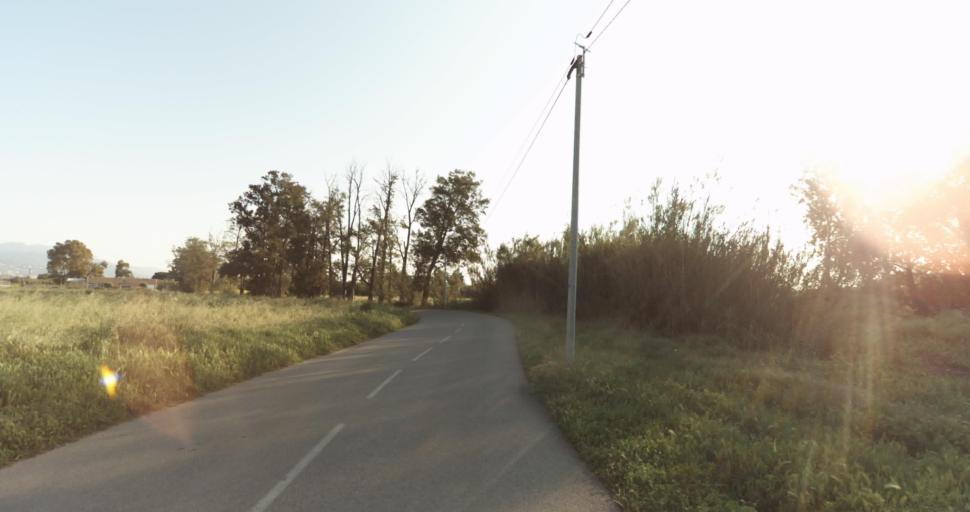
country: FR
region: Corsica
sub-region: Departement de la Haute-Corse
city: Biguglia
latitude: 42.6136
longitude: 9.4438
